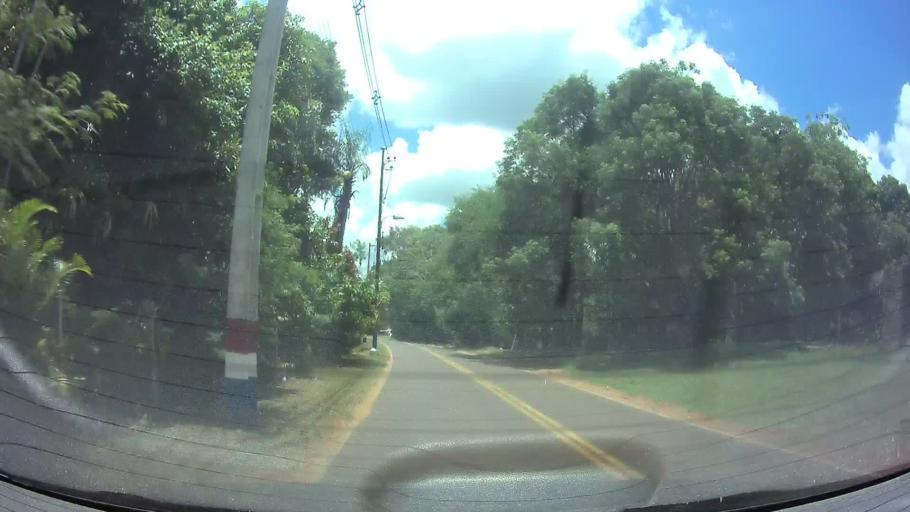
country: PY
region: Central
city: Capiata
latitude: -25.3225
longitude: -57.4276
